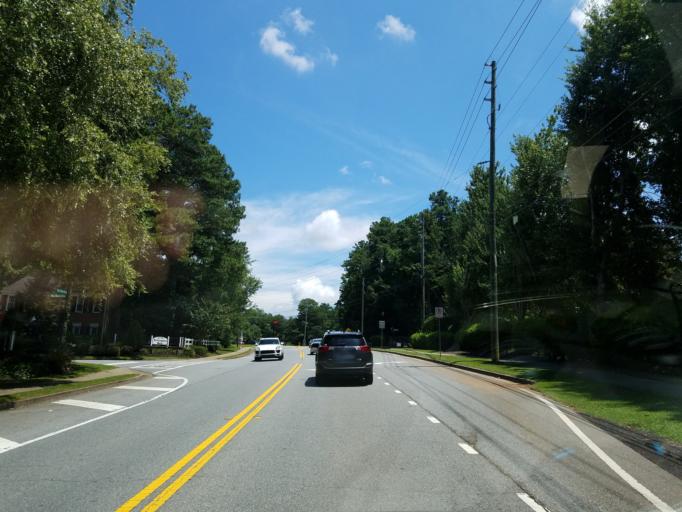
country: US
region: Georgia
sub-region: Fulton County
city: Johns Creek
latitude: 34.0654
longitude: -84.2278
